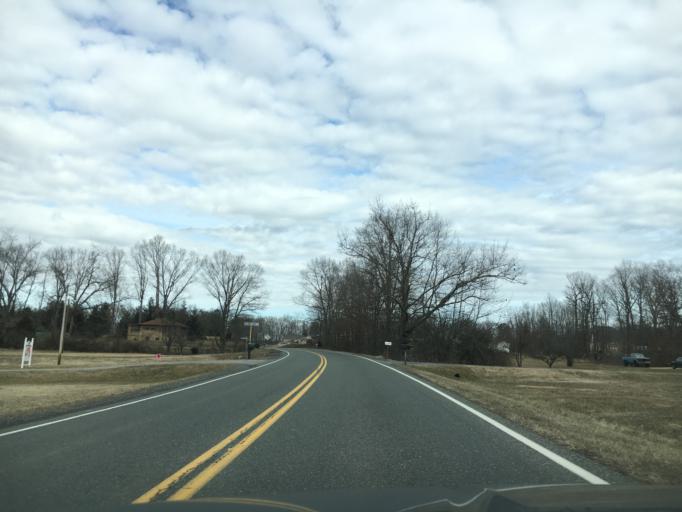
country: US
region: Virginia
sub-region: Augusta County
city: Dooms
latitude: 38.1293
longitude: -78.8459
